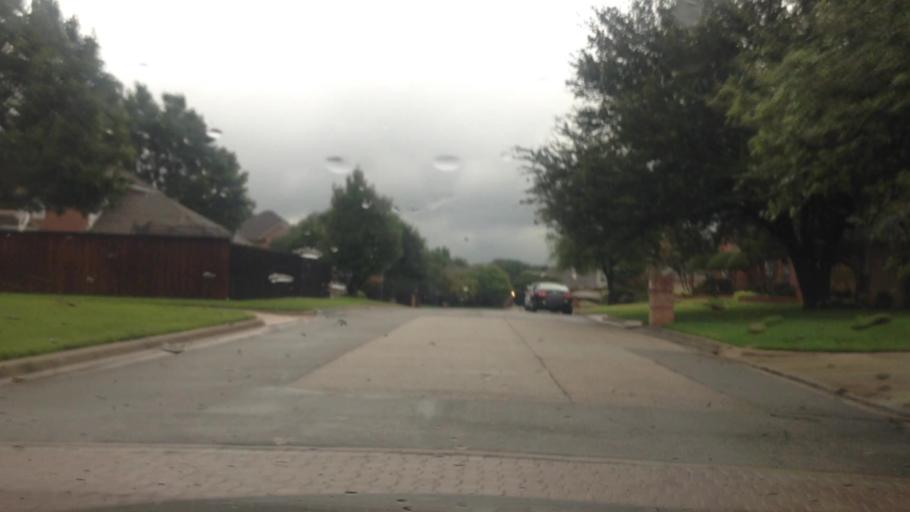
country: US
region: Texas
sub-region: Tarrant County
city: Colleyville
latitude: 32.8692
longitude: -97.1917
